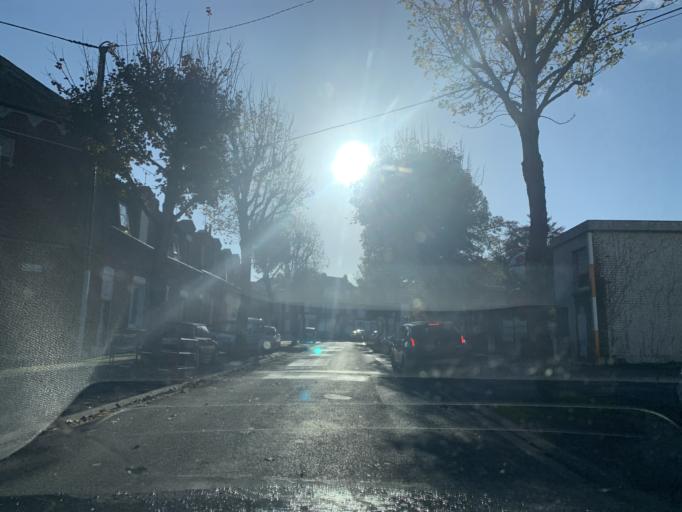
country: FR
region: Nord-Pas-de-Calais
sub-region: Departement du Nord
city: Cambrai
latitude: 50.1676
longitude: 3.2287
